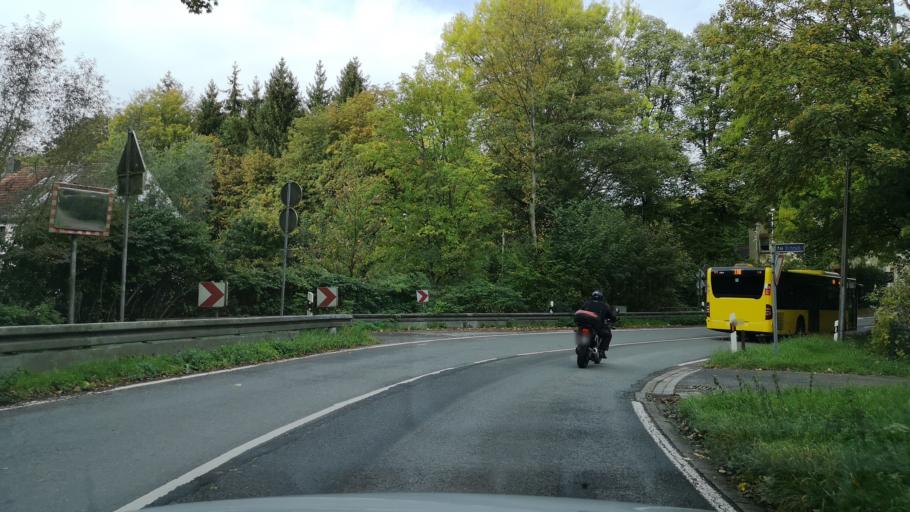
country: DE
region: North Rhine-Westphalia
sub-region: Regierungsbezirk Dusseldorf
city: Velbert
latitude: 51.3828
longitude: 7.0401
